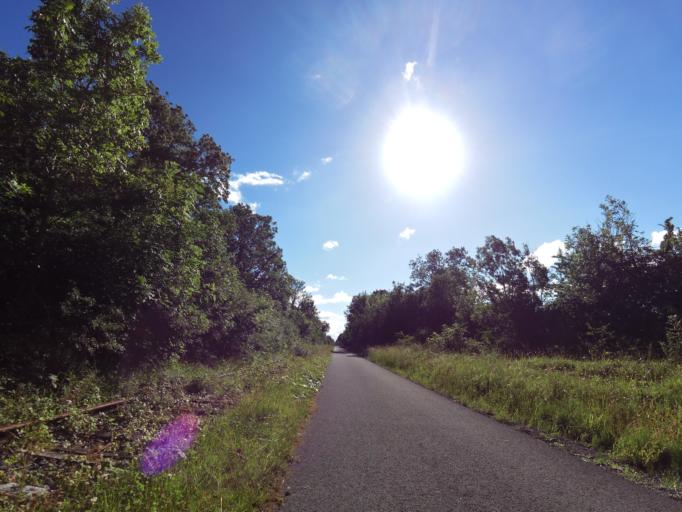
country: IE
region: Leinster
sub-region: Uibh Fhaili
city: Clara
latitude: 53.4278
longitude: -7.5955
